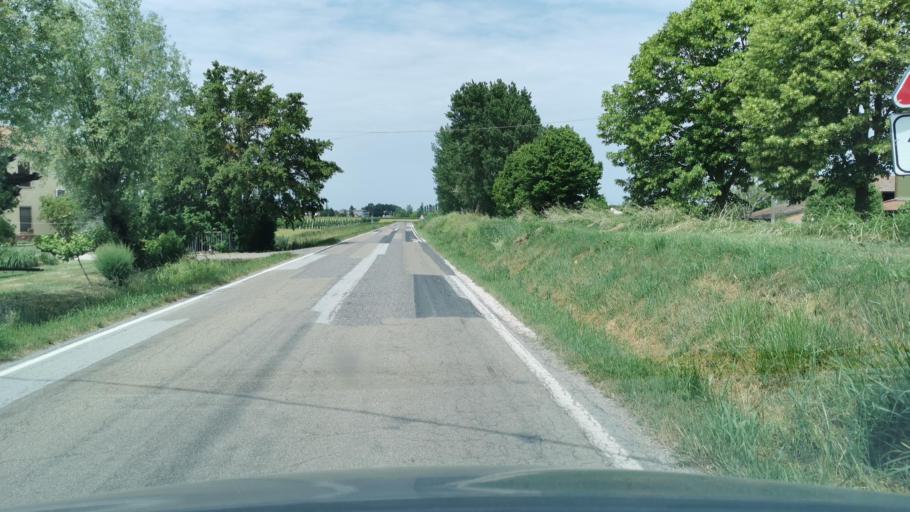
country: IT
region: Emilia-Romagna
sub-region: Provincia di Ravenna
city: Alfonsine
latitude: 44.4900
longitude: 12.0513
